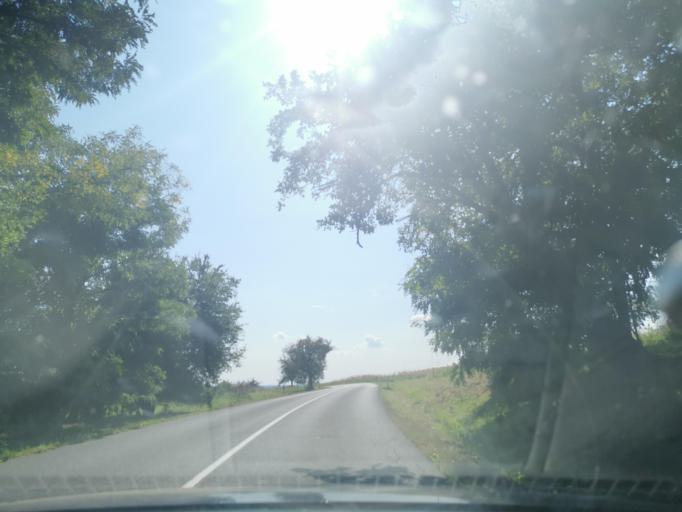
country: SK
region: Trnavsky
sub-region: Okres Senica
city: Senica
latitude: 48.6867
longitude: 17.2723
